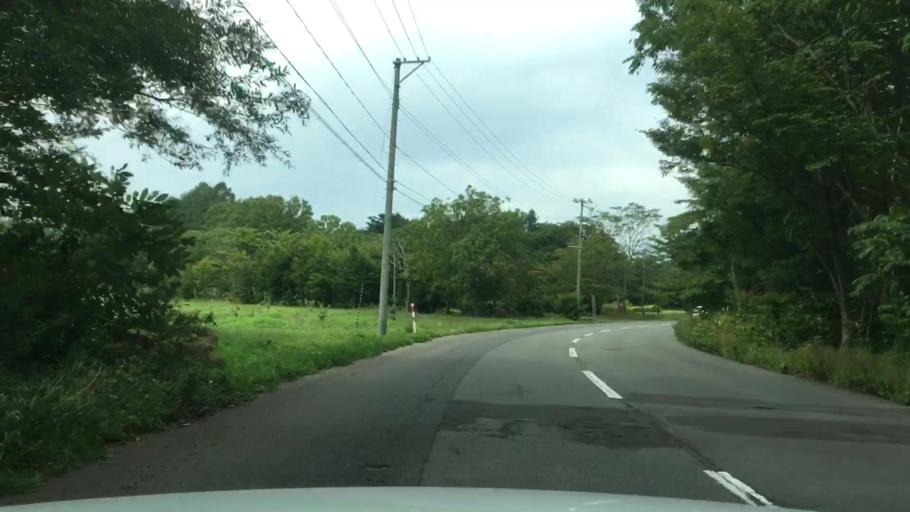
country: JP
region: Aomori
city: Shimokizukuri
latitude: 40.6871
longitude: 140.3641
